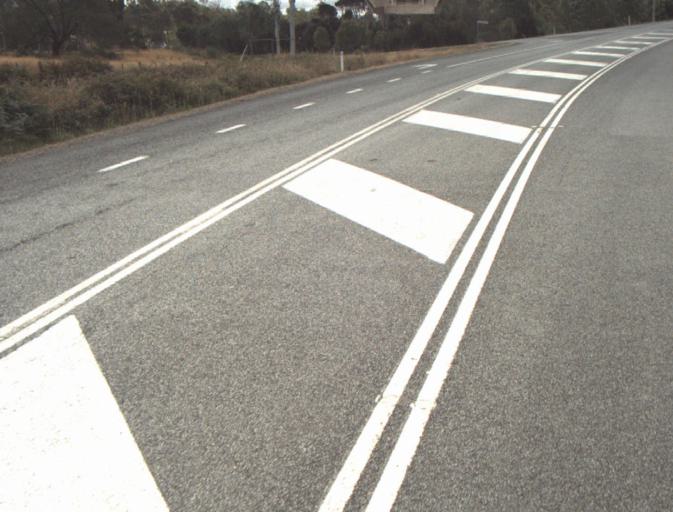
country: AU
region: Tasmania
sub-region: Launceston
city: Mayfield
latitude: -41.3069
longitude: 147.0490
